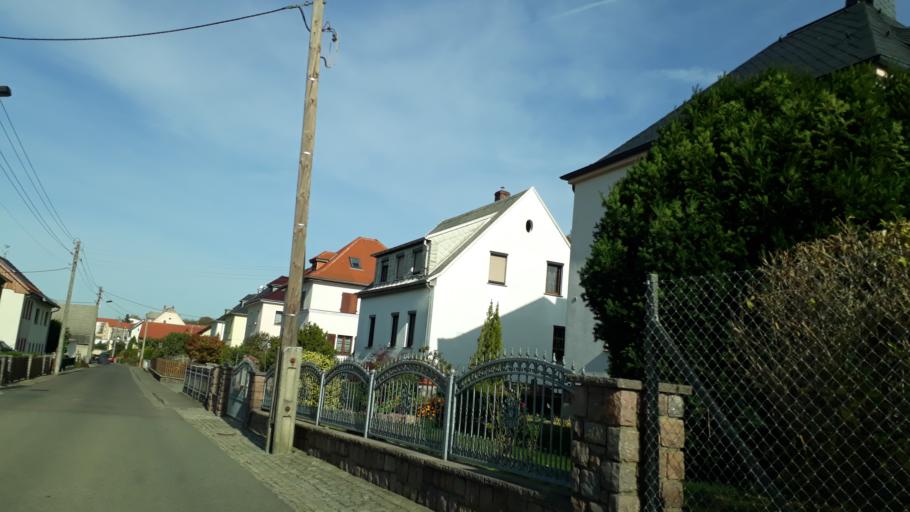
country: DE
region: Saxony
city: Dobeln
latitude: 51.1143
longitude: 13.1361
